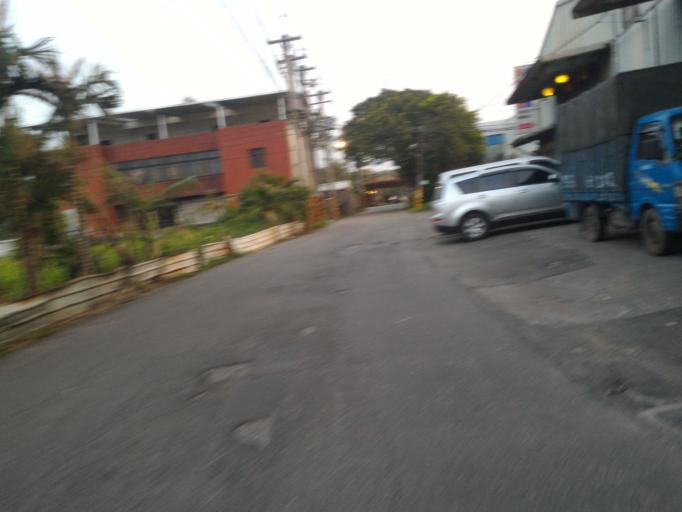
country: TW
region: Taiwan
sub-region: Taoyuan
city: Taoyuan
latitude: 24.9497
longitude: 121.4014
